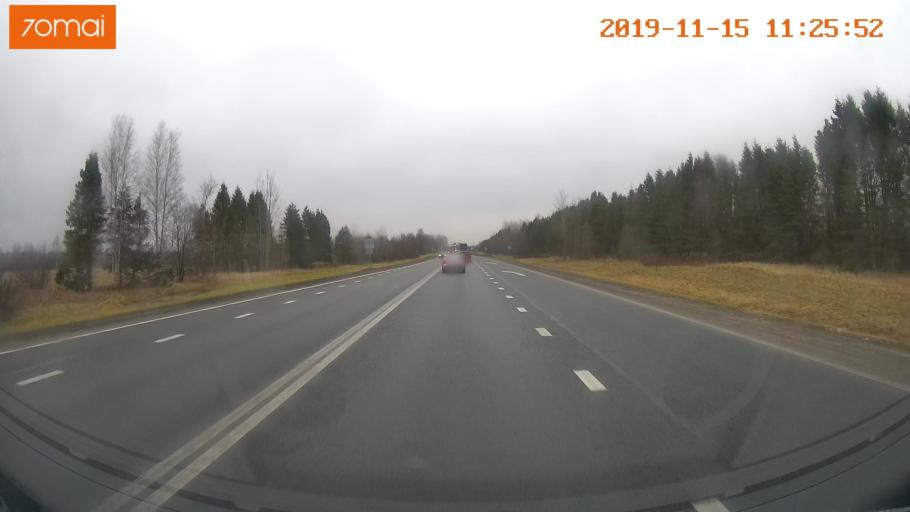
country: RU
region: Vologda
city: Molochnoye
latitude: 59.1642
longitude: 39.4339
